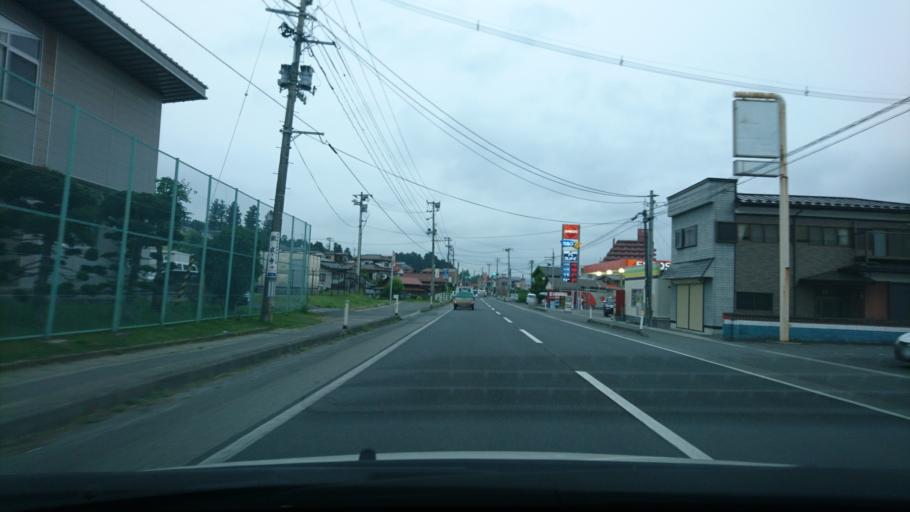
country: JP
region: Iwate
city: Ichinoseki
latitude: 38.9159
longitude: 141.1317
